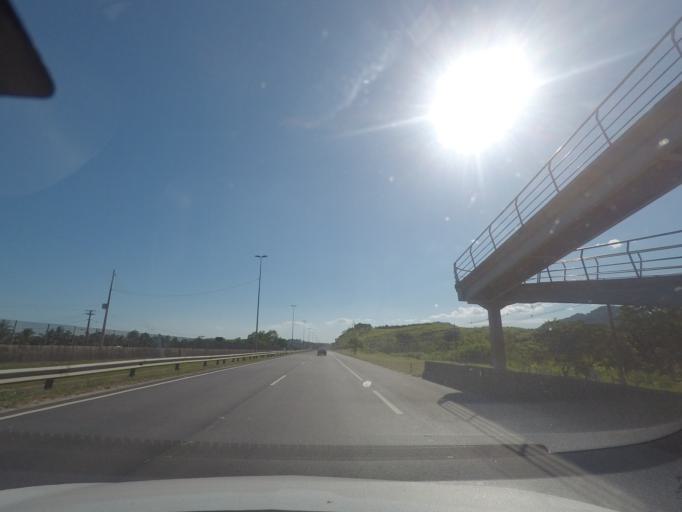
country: BR
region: Rio de Janeiro
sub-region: Guapimirim
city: Guapimirim
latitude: -22.6456
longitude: -43.0696
